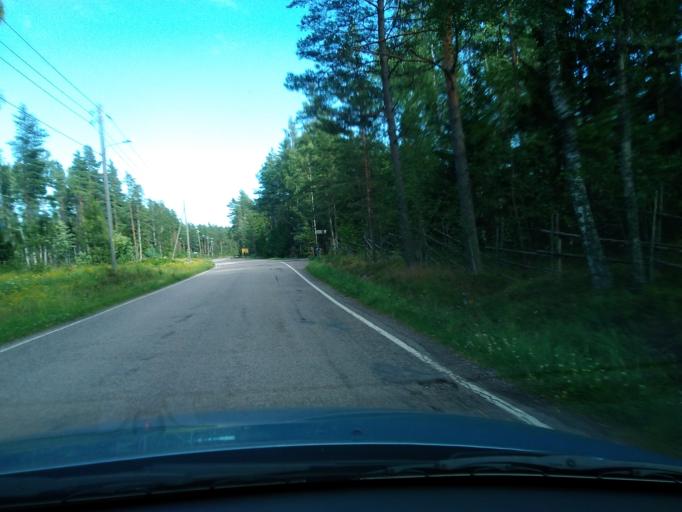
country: FI
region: Uusimaa
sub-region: Raaseporin
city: Hanko
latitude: 59.8407
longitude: 23.0820
